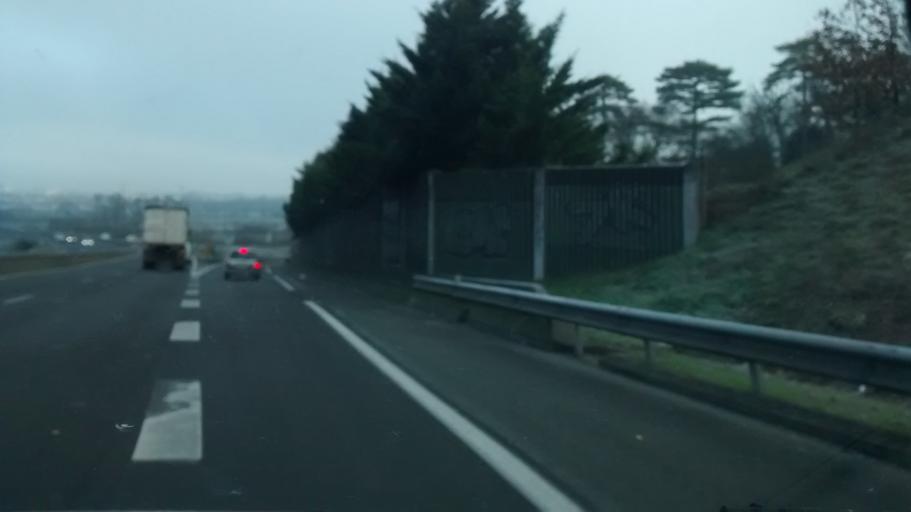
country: FR
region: Centre
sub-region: Departement d'Indre-et-Loire
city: Joue-les-Tours
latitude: 47.3656
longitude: 0.6518
